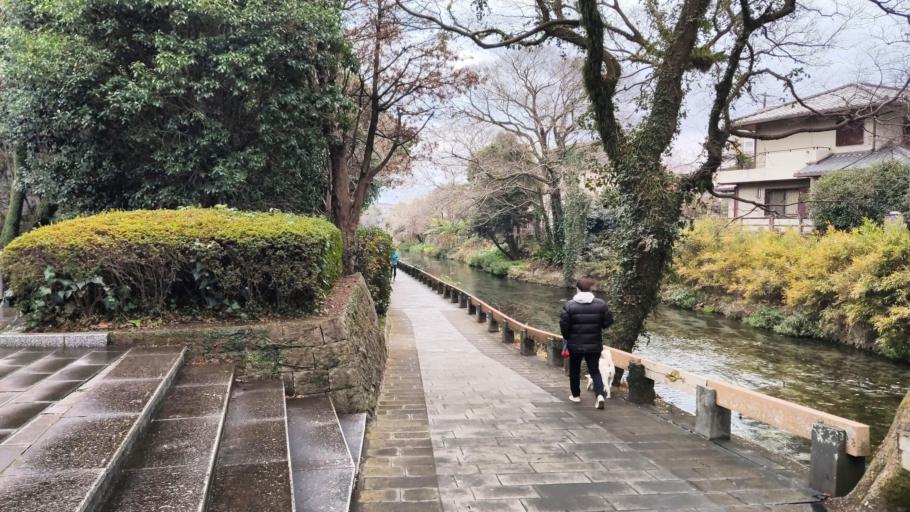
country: JP
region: Kumamoto
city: Kumamoto
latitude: 32.7870
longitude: 130.7347
